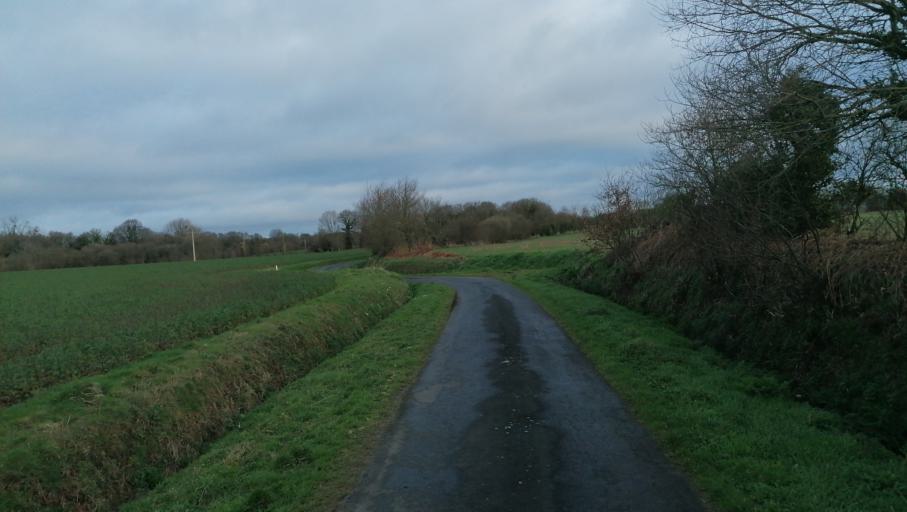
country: FR
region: Brittany
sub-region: Departement des Cotes-d'Armor
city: Pommerit-le-Vicomte
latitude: 48.6413
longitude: -3.0688
